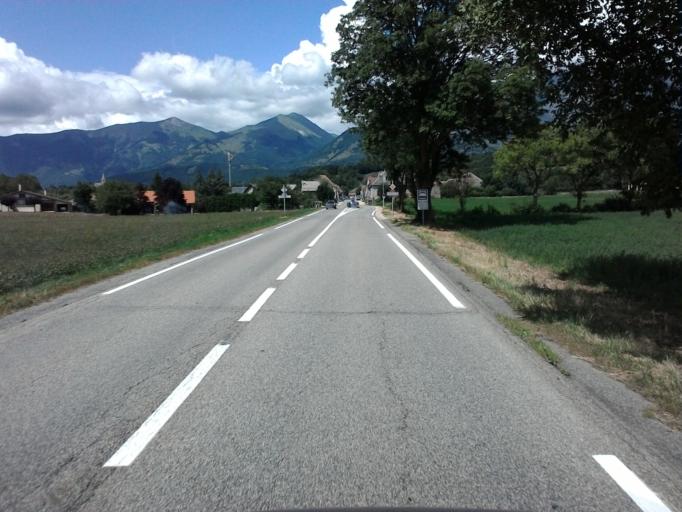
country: FR
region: Provence-Alpes-Cote d'Azur
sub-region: Departement des Hautes-Alpes
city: Saint-Bonnet-en-Champsaur
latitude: 44.7498
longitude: 6.0084
